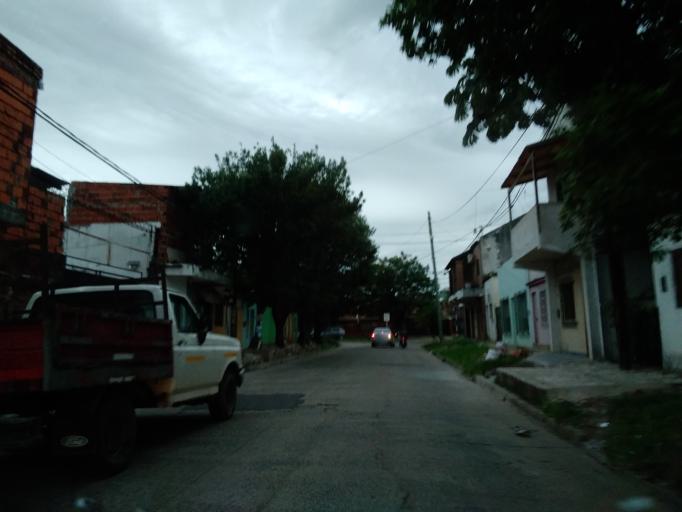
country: AR
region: Corrientes
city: Corrientes
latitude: -27.4786
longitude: -58.8212
